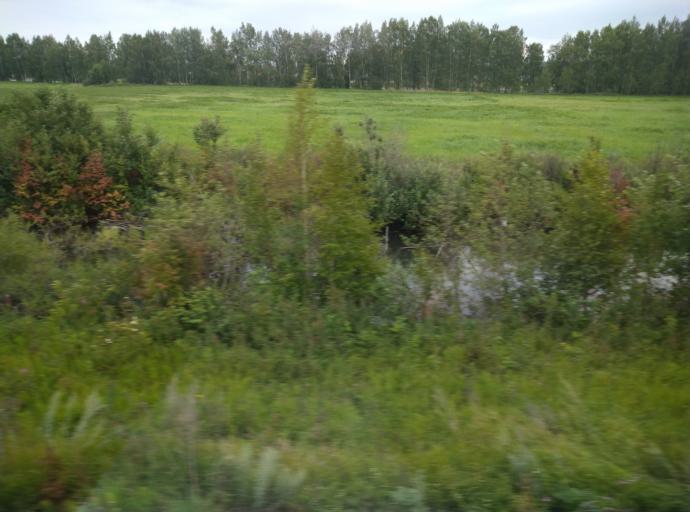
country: RU
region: Kostroma
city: Nerekhta
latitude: 57.4866
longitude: 40.5993
